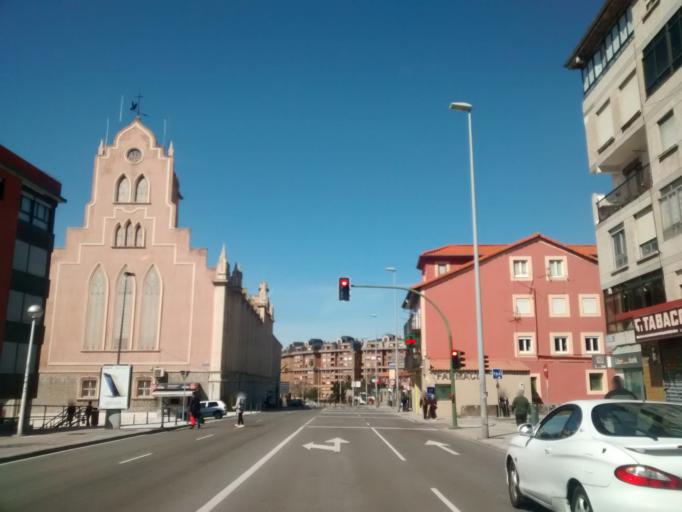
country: ES
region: Cantabria
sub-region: Provincia de Cantabria
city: Santander
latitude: 43.4673
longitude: -3.8075
